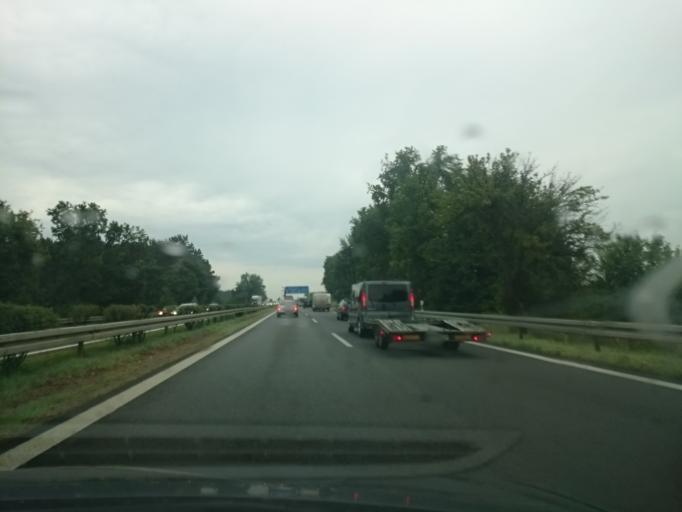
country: DE
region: Brandenburg
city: Gross Kreutz
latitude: 52.3539
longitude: 12.8151
